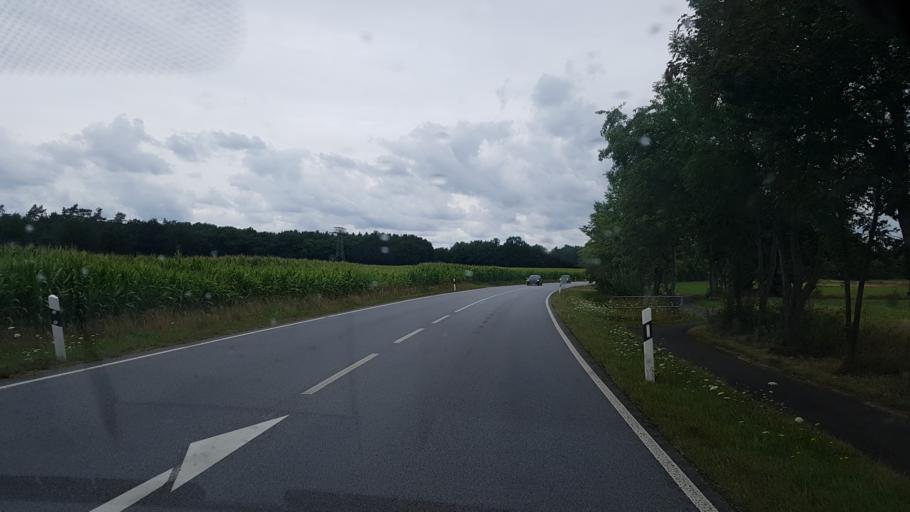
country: DE
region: Saxony
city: Niesky
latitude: 51.2628
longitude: 14.8083
